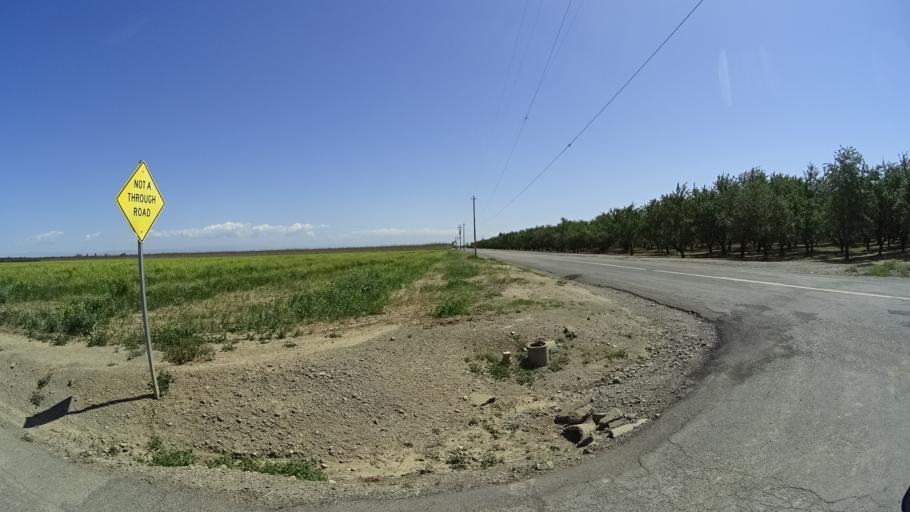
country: US
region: California
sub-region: Glenn County
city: Orland
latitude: 39.6965
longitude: -122.1638
